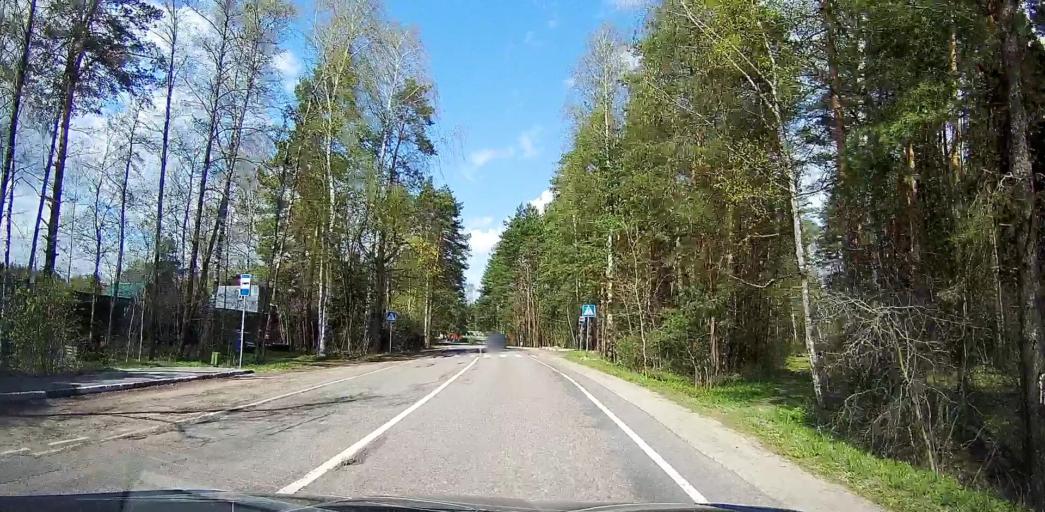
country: RU
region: Moskovskaya
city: Davydovo
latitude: 55.5703
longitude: 38.8232
